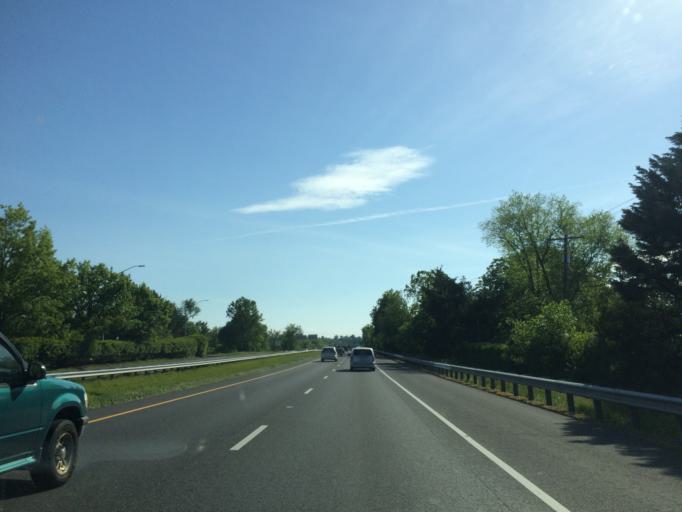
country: US
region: Maryland
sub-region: Frederick County
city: Frederick
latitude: 39.4266
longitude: -77.4237
